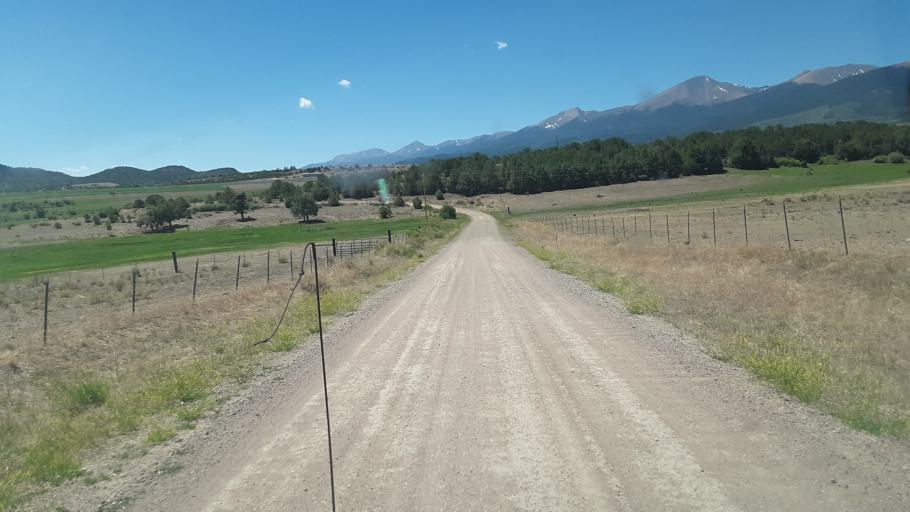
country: US
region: Colorado
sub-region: Custer County
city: Westcliffe
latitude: 38.3008
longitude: -105.6155
